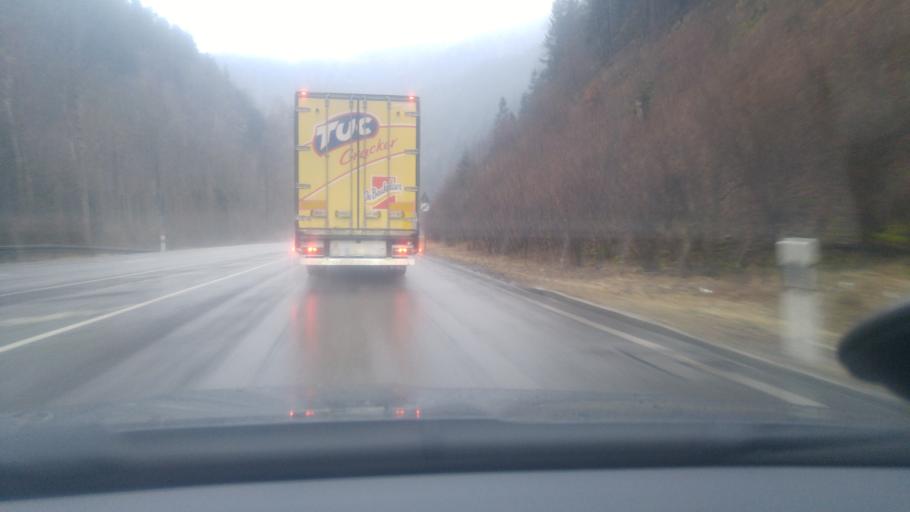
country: DE
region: Baden-Wuerttemberg
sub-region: Freiburg Region
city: Buchenbach
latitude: 47.9260
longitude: 8.0311
